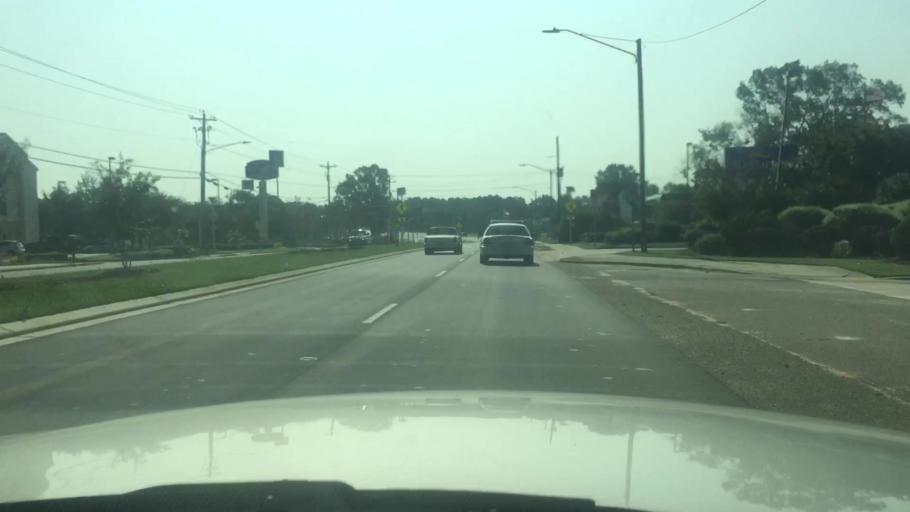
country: US
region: North Carolina
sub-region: Cumberland County
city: Vander
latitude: 35.0090
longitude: -78.8274
